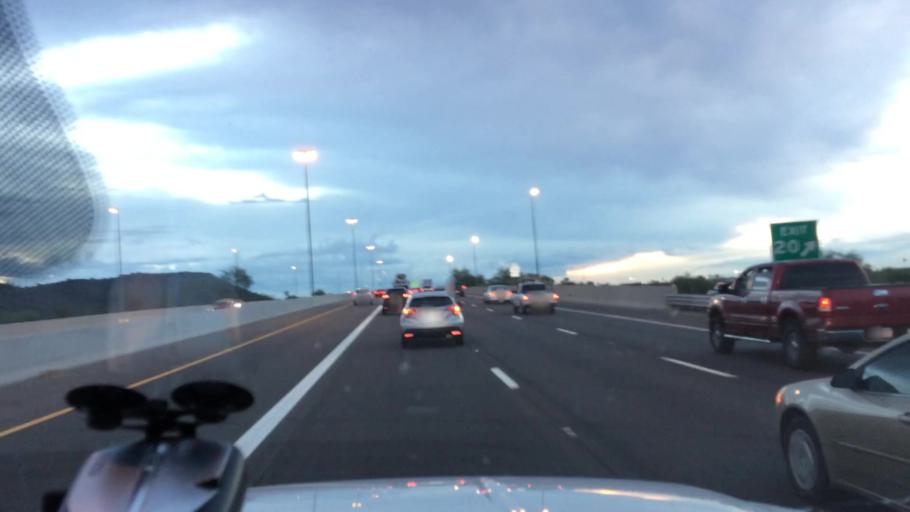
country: US
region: Arizona
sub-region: Maricopa County
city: Peoria
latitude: 33.6681
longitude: -112.1748
